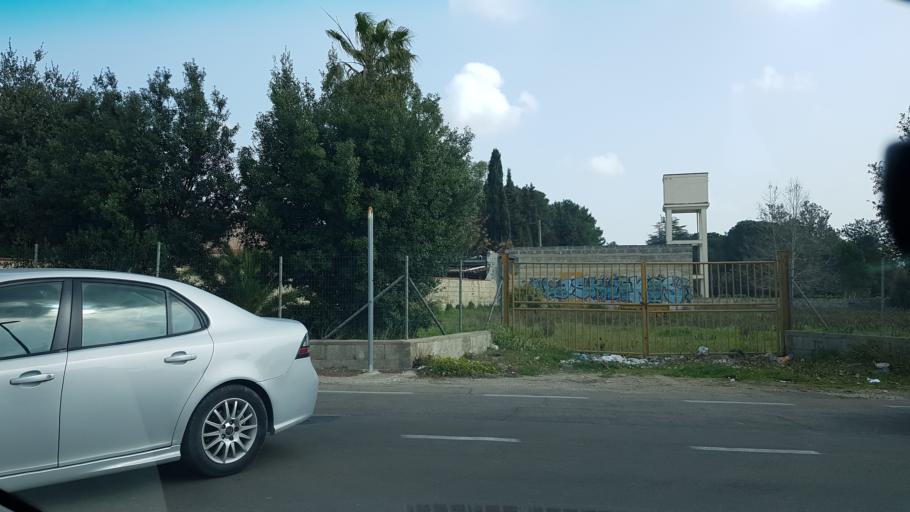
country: IT
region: Apulia
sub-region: Provincia di Lecce
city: Castromediano
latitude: 40.3257
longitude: 18.1826
